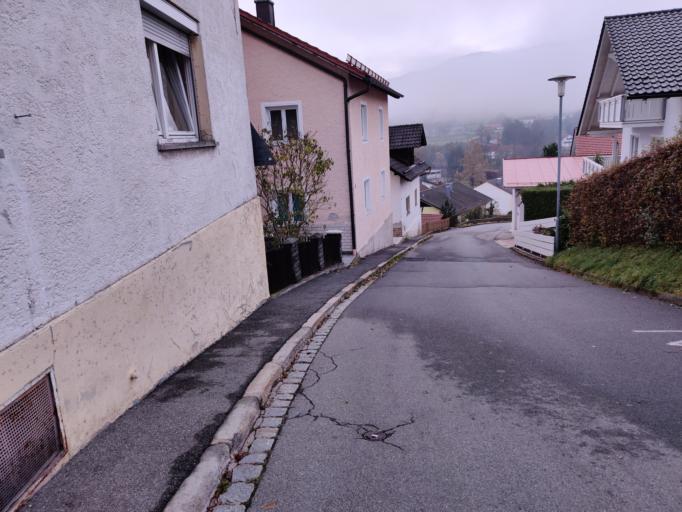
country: DE
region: Bavaria
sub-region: Upper Palatinate
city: Lam
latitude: 49.1949
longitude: 13.0535
